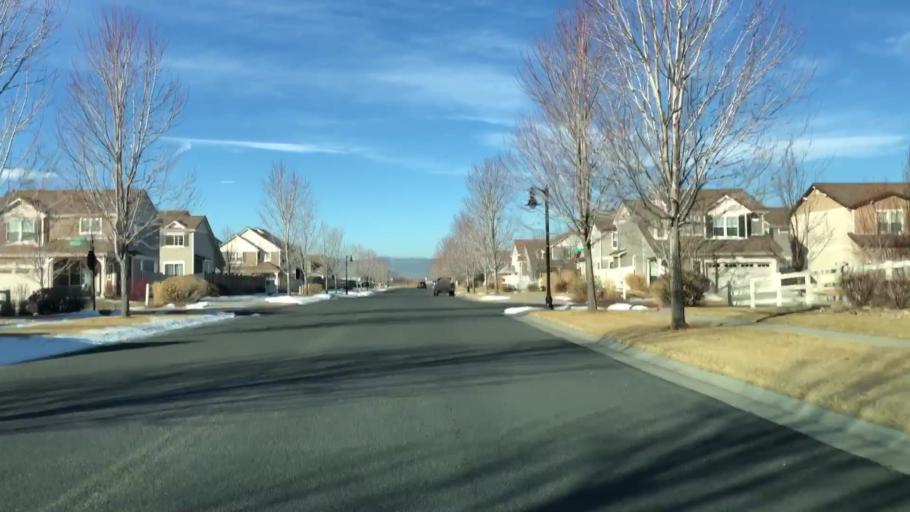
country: US
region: Colorado
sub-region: Larimer County
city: Loveland
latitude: 40.3907
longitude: -104.9872
